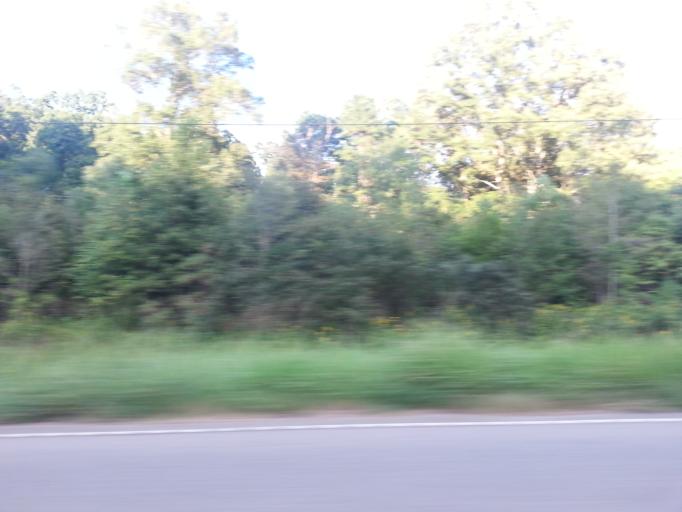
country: US
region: Tennessee
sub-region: Jefferson County
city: Jefferson City
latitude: 36.1449
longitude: -83.5266
